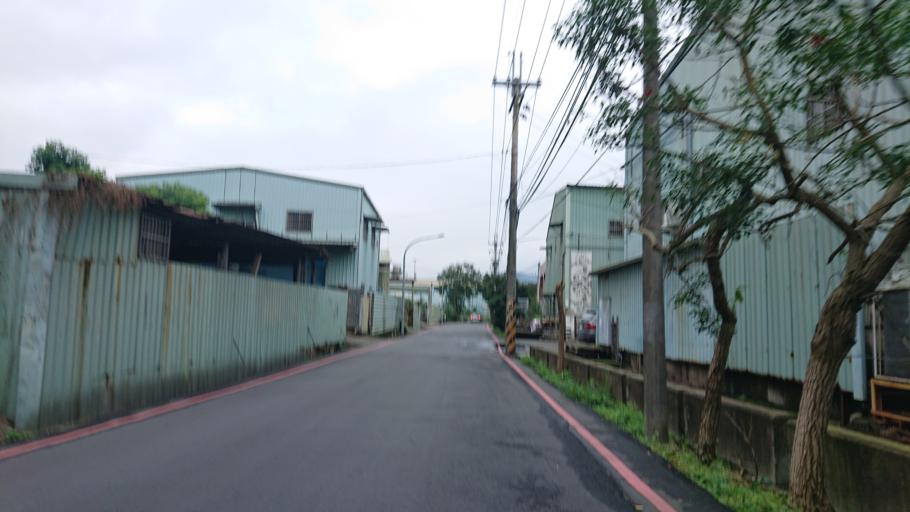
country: TW
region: Taiwan
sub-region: Taoyuan
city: Taoyuan
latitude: 24.9491
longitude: 121.3875
